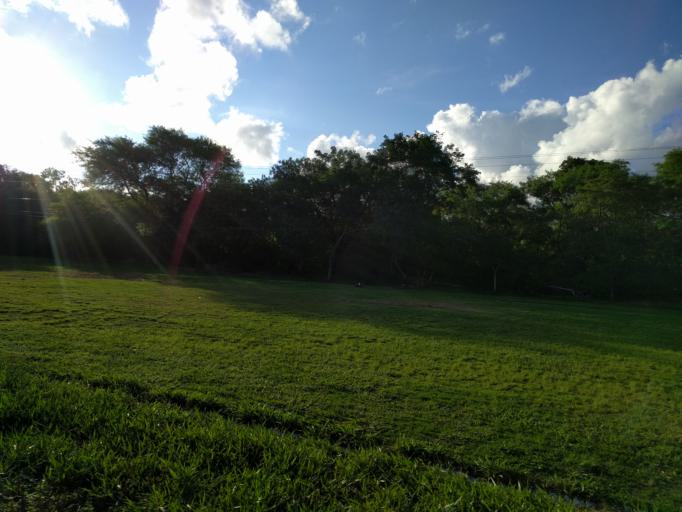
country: BO
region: Santa Cruz
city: Santa Cruz de la Sierra
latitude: -17.7730
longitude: -63.2128
